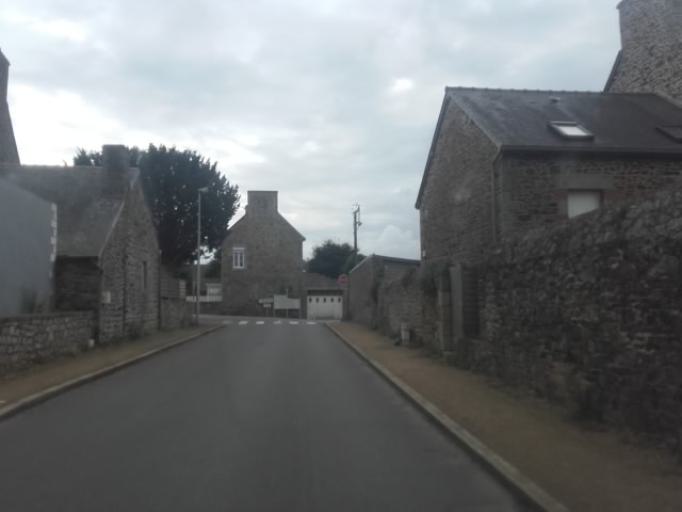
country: FR
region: Brittany
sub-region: Departement des Cotes-d'Armor
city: Tremuson
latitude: 48.5547
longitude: -2.8588
